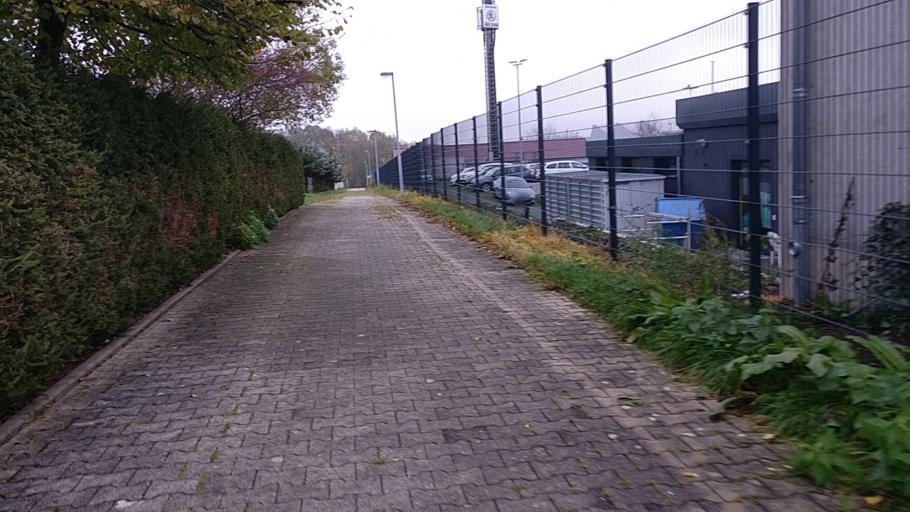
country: DE
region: Saxony
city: Gornau
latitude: 50.7880
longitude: 12.9933
